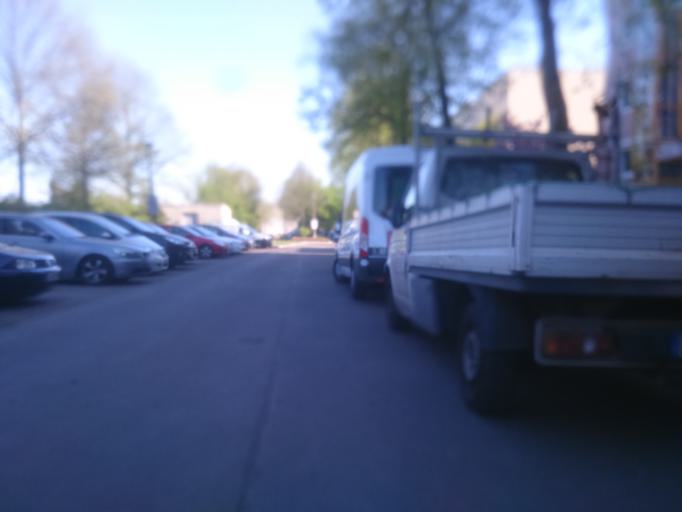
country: DE
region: Berlin
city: Neu-Hohenschoenhausen
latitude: 52.5611
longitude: 13.5138
